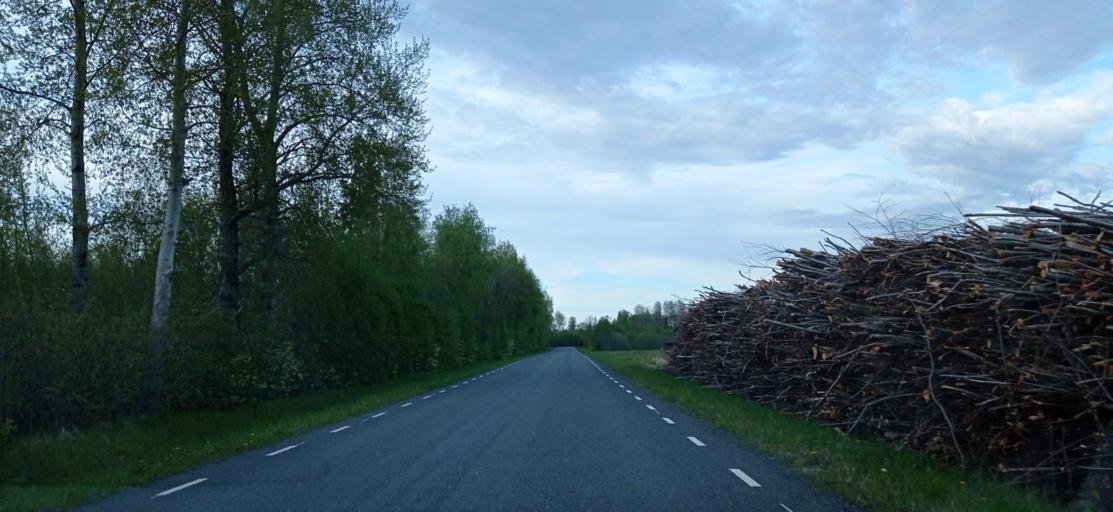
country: EE
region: Paernumaa
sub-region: Tootsi vald
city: Tootsi
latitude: 58.5636
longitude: 24.8033
